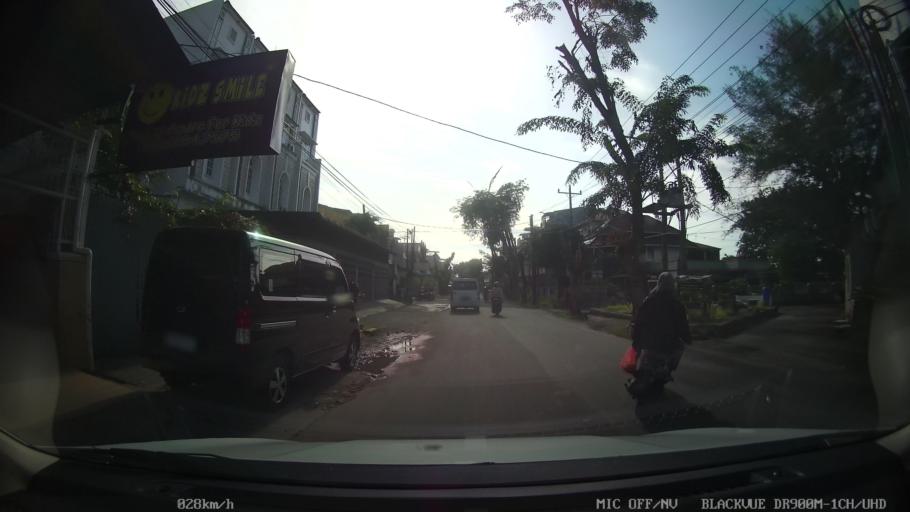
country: ID
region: North Sumatra
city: Medan
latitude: 3.6042
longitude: 98.6552
